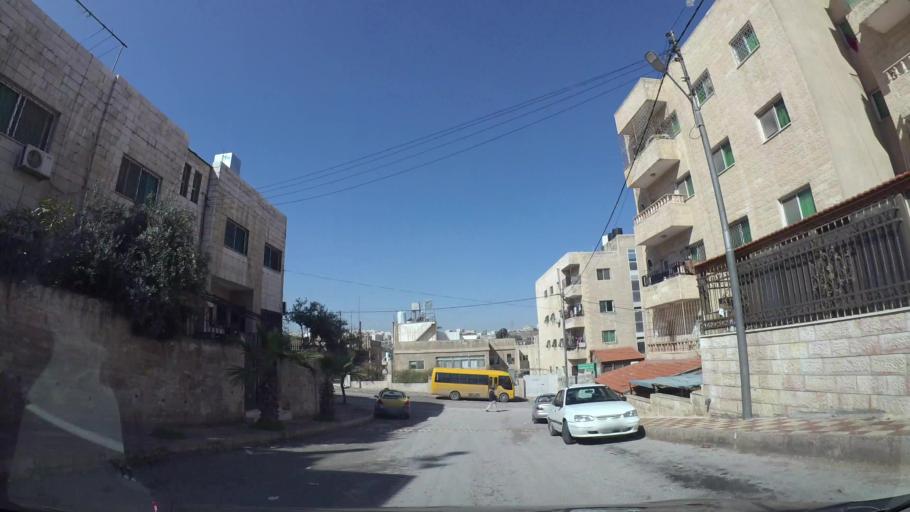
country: JO
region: Amman
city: Amman
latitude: 31.9912
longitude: 35.9843
